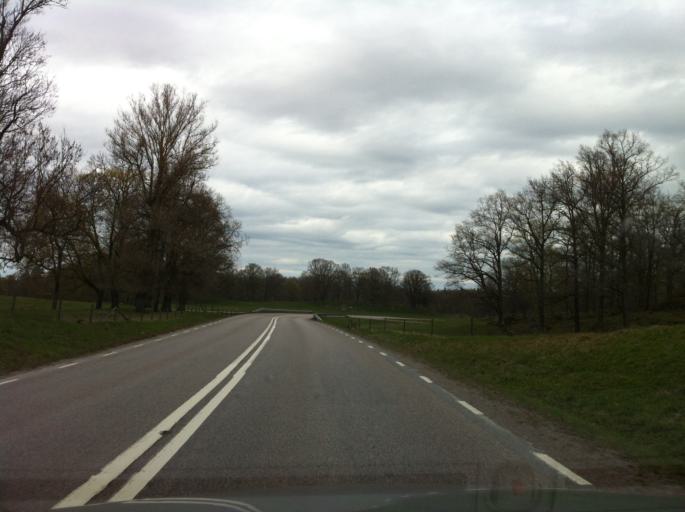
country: SE
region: OEstergoetland
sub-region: Atvidabergs Kommun
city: Atvidaberg
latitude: 58.0903
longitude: 15.8984
